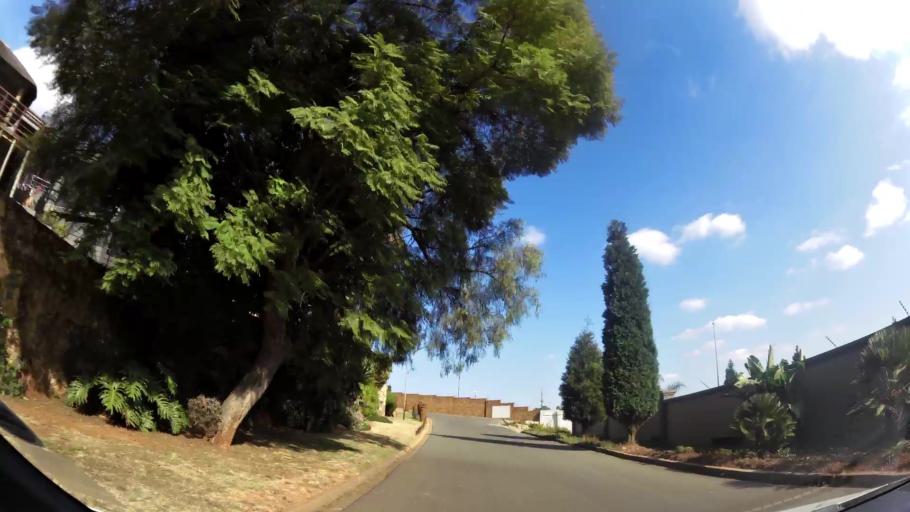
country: ZA
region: Gauteng
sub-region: Ekurhuleni Metropolitan Municipality
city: Germiston
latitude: -26.1942
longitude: 28.1329
